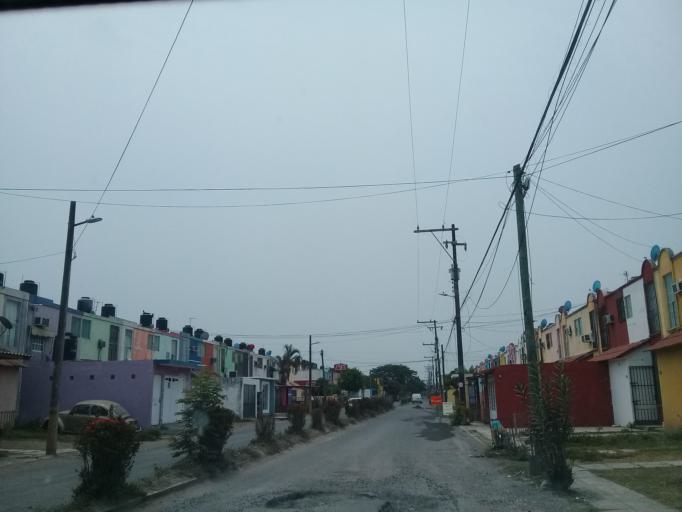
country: MX
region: Veracruz
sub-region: Veracruz
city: Las Amapolas
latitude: 19.1569
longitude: -96.2065
